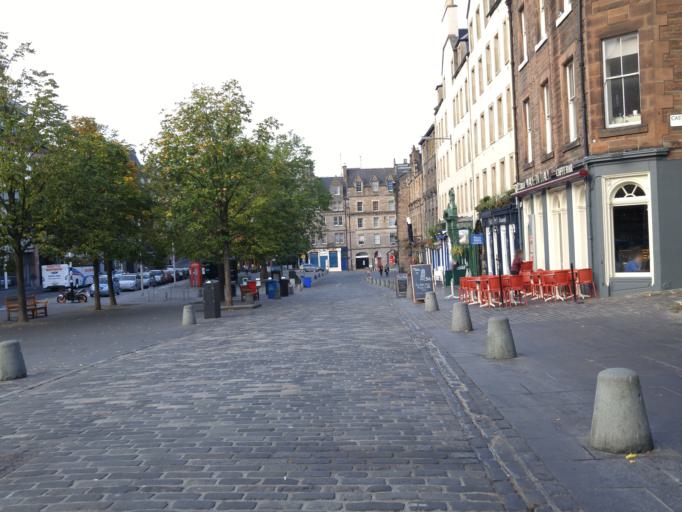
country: GB
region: Scotland
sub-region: Edinburgh
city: Edinburgh
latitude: 55.9476
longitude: -3.1962
